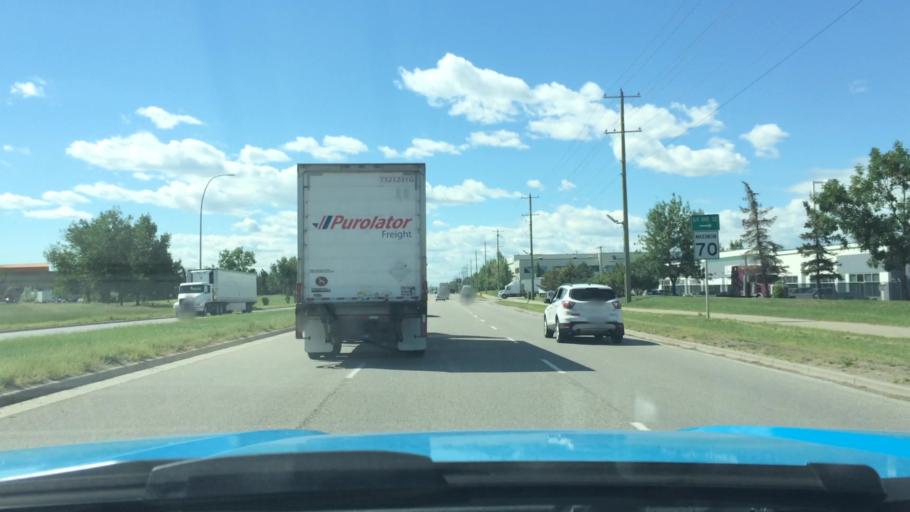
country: CA
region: Alberta
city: Calgary
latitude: 50.9985
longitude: -113.9587
